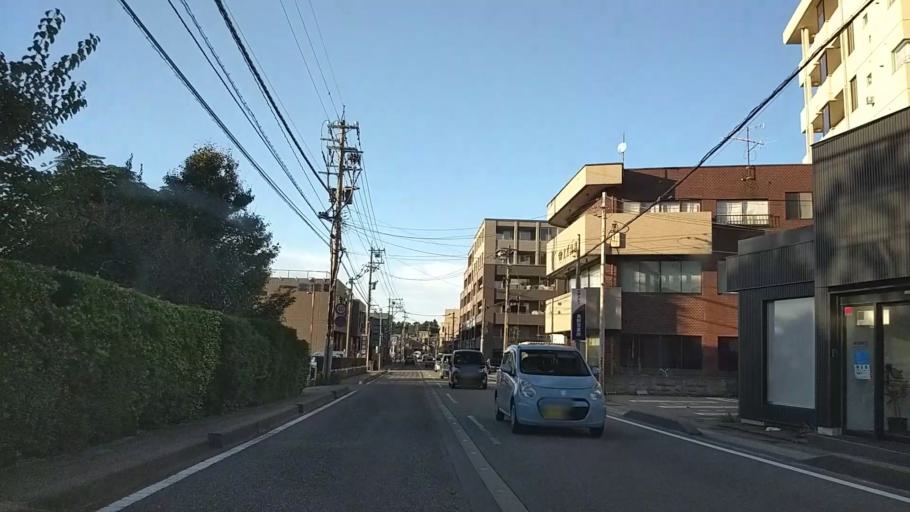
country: JP
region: Ishikawa
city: Nonoichi
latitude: 36.5463
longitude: 136.6490
